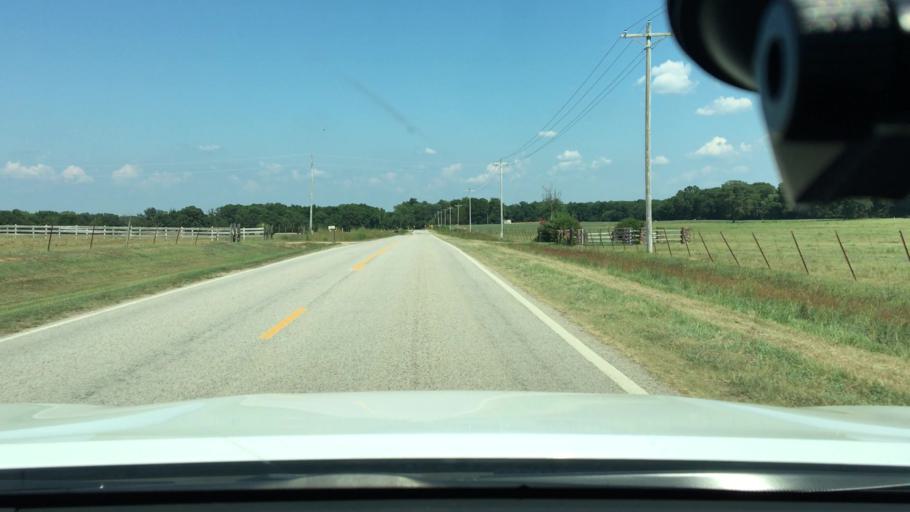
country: US
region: Arkansas
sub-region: Johnson County
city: Coal Hill
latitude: 35.3508
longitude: -93.5743
